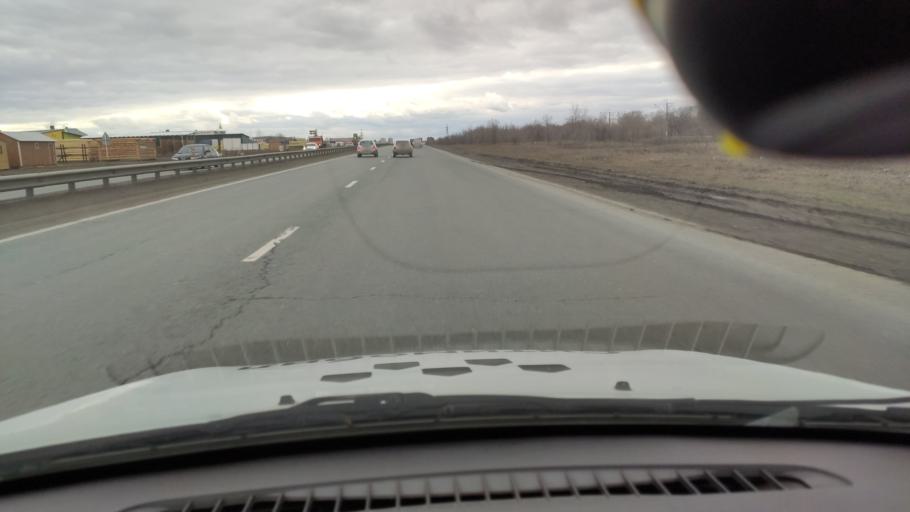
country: RU
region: Samara
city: Tol'yatti
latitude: 53.5680
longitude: 49.3764
